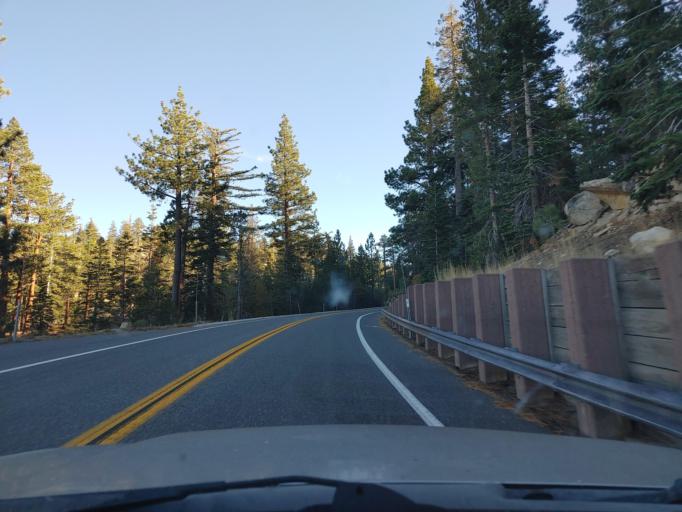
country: US
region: California
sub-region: Placer County
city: Tahoma
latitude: 38.9884
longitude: -120.1087
